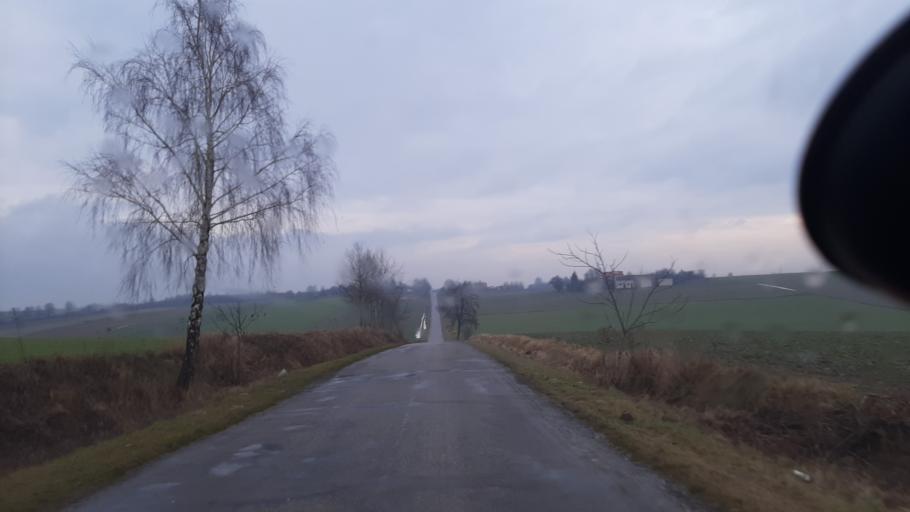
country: PL
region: Lublin Voivodeship
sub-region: Powiat lubelski
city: Niemce
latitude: 51.3212
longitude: 22.5904
